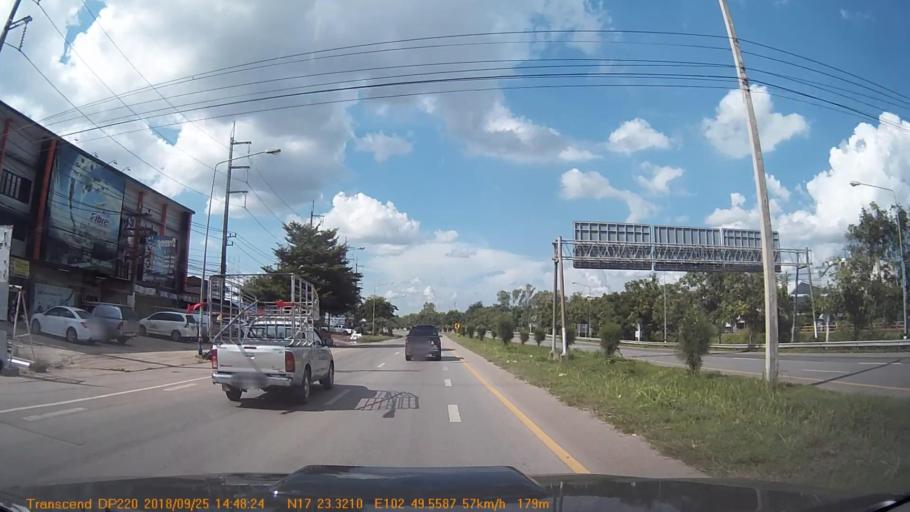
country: TH
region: Changwat Udon Thani
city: Udon Thani
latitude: 17.3890
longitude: 102.8260
